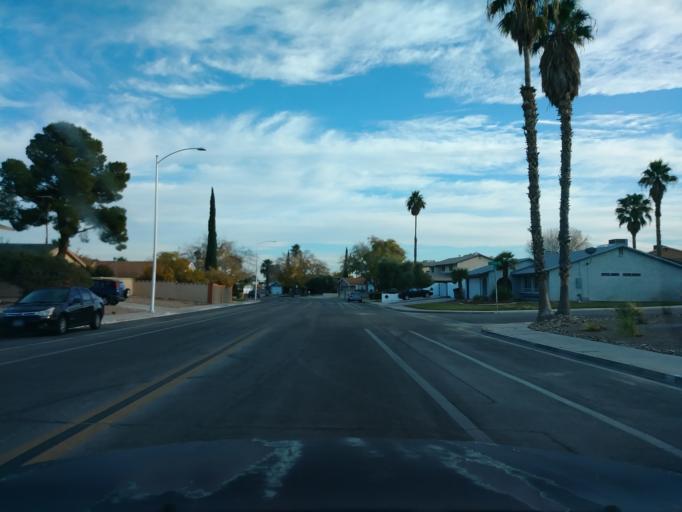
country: US
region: Nevada
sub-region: Clark County
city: Spring Valley
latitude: 36.1692
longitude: -115.2375
